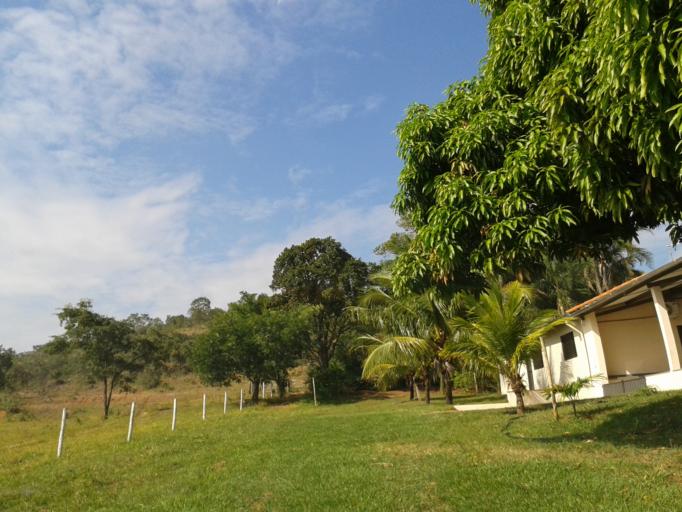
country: BR
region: Minas Gerais
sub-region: Campina Verde
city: Campina Verde
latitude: -19.3970
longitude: -49.6258
